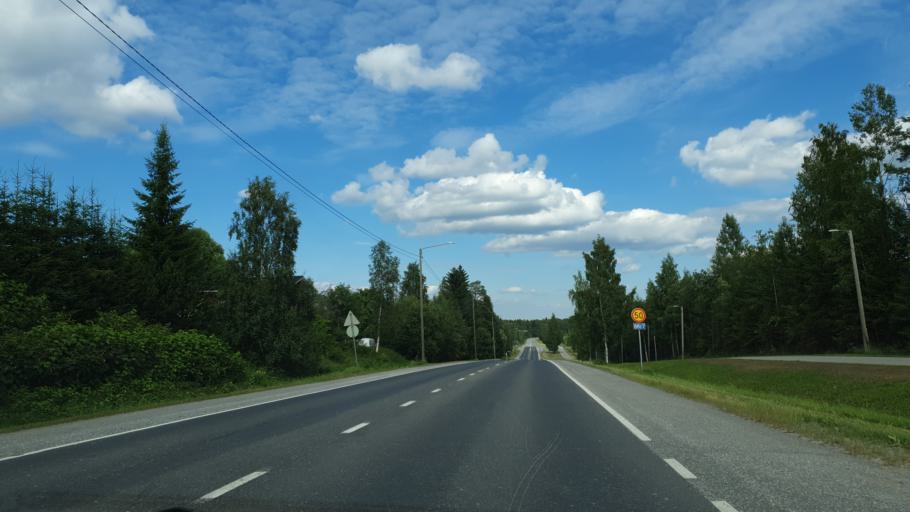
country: FI
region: Kainuu
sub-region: Kajaani
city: Kajaani
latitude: 64.2416
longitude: 27.7554
